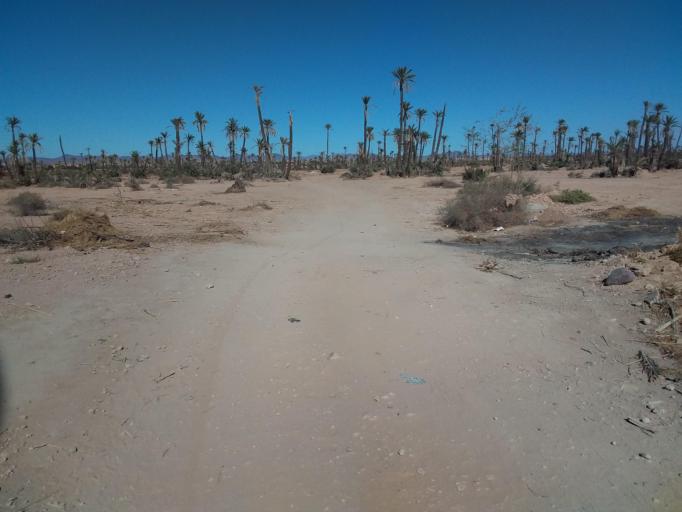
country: MA
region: Marrakech-Tensift-Al Haouz
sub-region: Marrakech
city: Marrakesh
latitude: 31.6788
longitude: -7.9519
